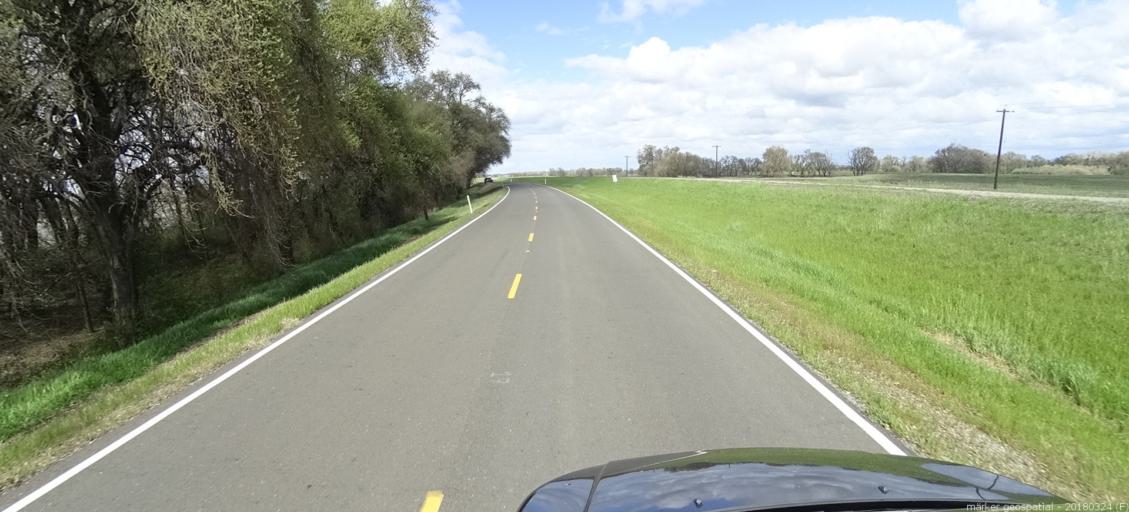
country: US
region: California
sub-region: Sacramento County
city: Elverta
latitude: 38.7181
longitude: -121.6047
